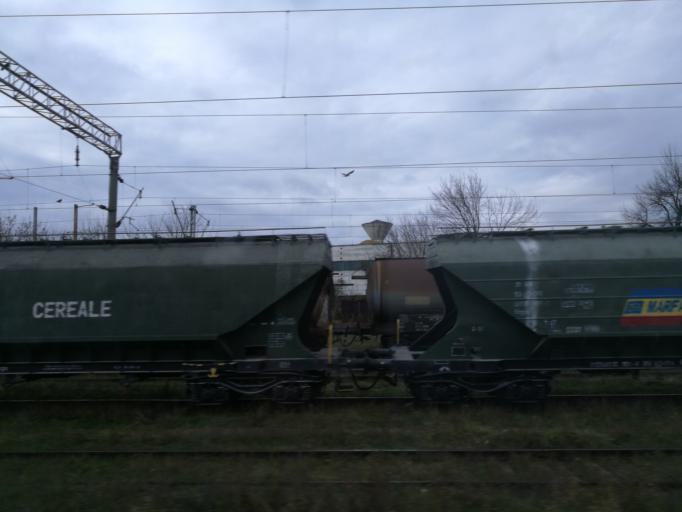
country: RO
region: Neamt
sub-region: Municipiul Roman
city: Roman
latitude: 46.9430
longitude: 26.9173
